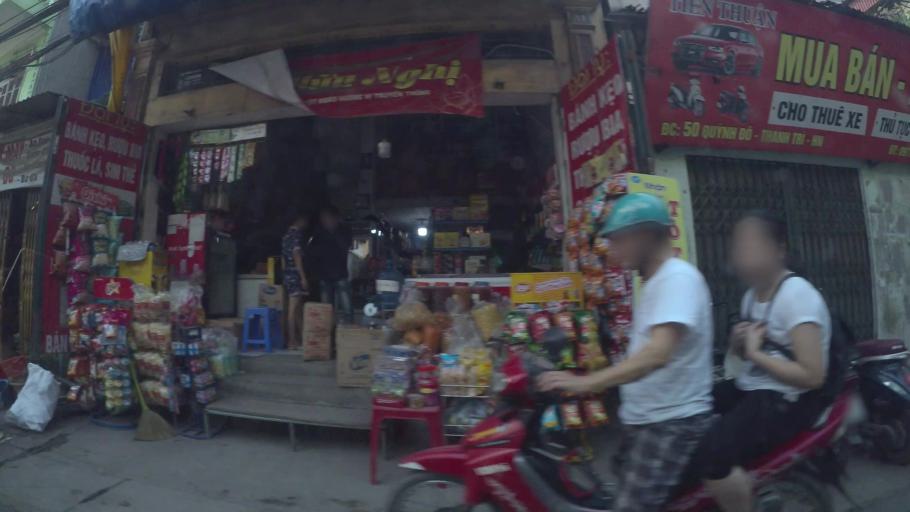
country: VN
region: Ha Noi
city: Van Dien
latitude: 20.9394
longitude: 105.8401
